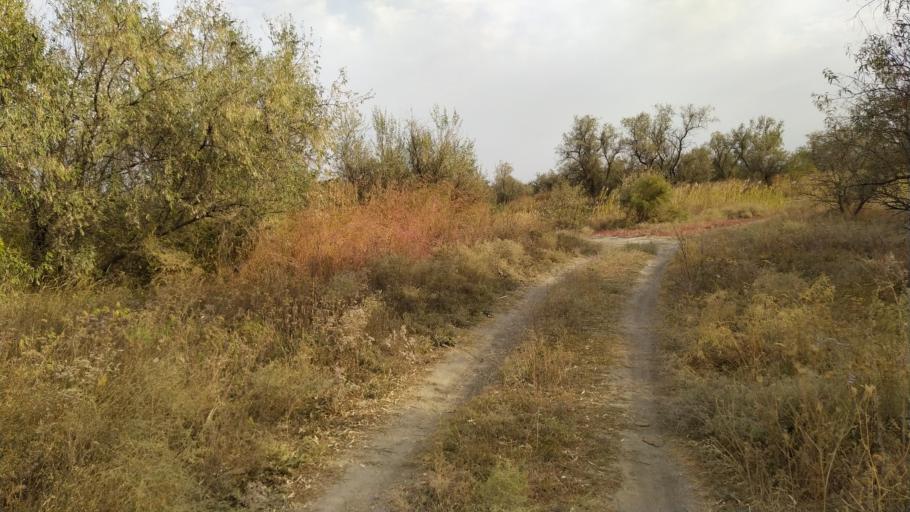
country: RU
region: Rostov
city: Kuleshovka
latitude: 47.1393
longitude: 39.5818
